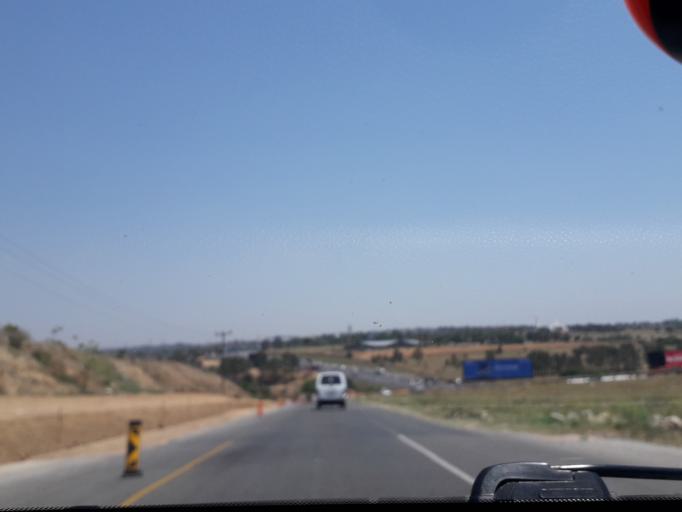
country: ZA
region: Gauteng
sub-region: City of Johannesburg Metropolitan Municipality
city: Midrand
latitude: -26.0269
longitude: 28.1127
